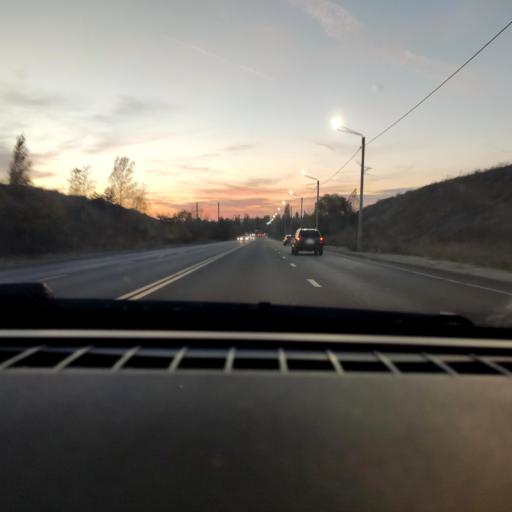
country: RU
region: Voronezj
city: Maslovka
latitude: 51.6213
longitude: 39.2682
